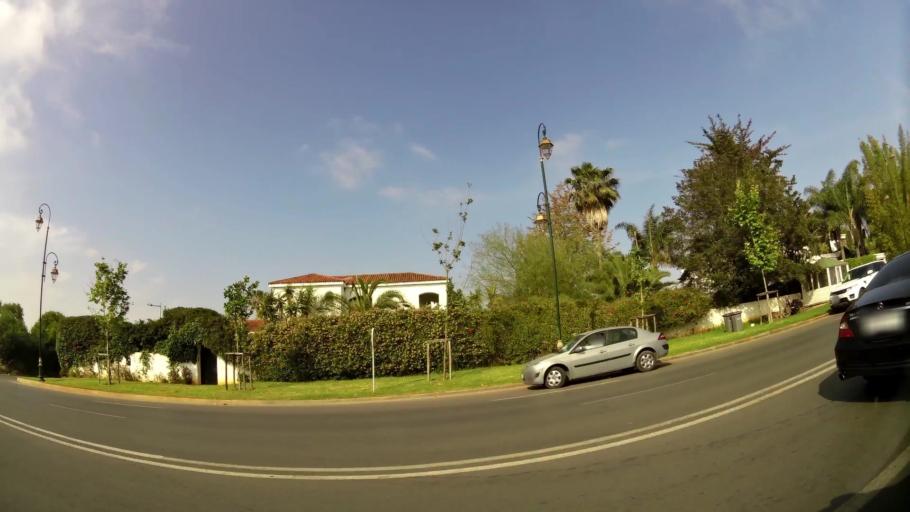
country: MA
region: Rabat-Sale-Zemmour-Zaer
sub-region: Rabat
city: Rabat
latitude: 33.9475
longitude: -6.8109
